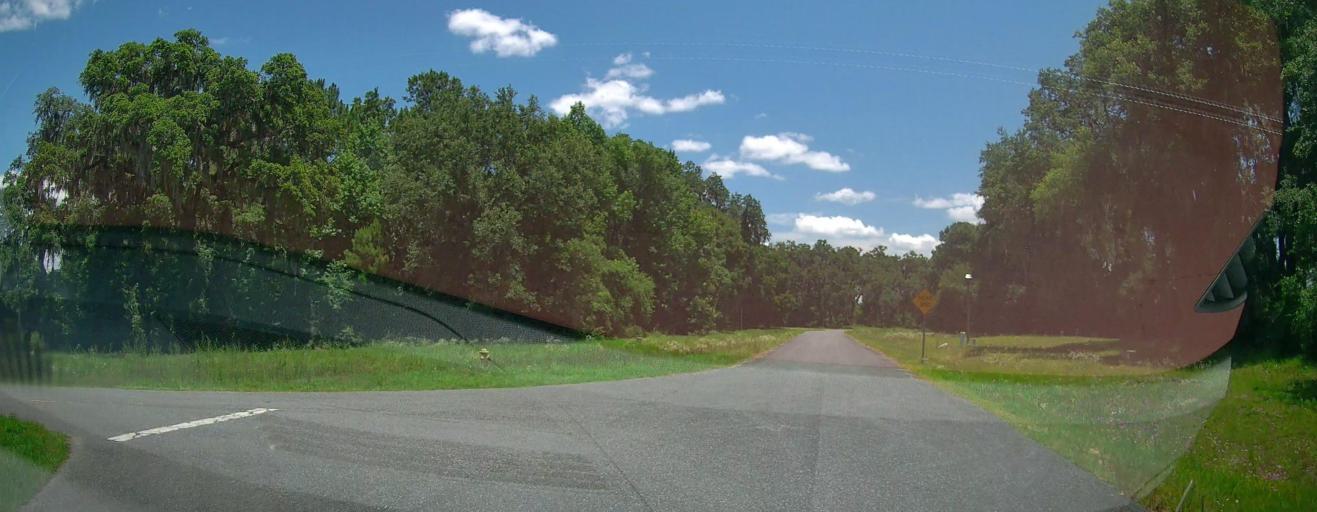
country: US
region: Florida
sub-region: Marion County
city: Belleview
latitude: 29.0893
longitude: -82.0752
